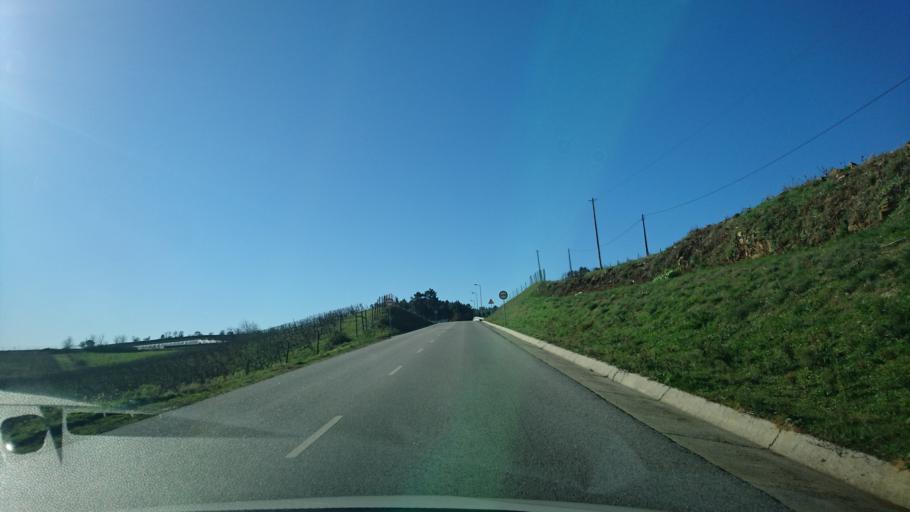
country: PT
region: Braganca
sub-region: Braganca Municipality
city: Vila Flor
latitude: 41.3063
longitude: -7.1608
